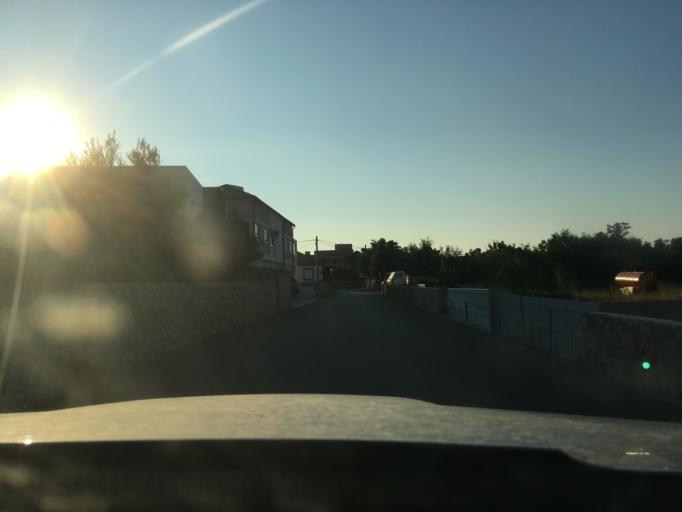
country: HR
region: Zadarska
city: Vir
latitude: 44.3046
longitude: 15.0792
